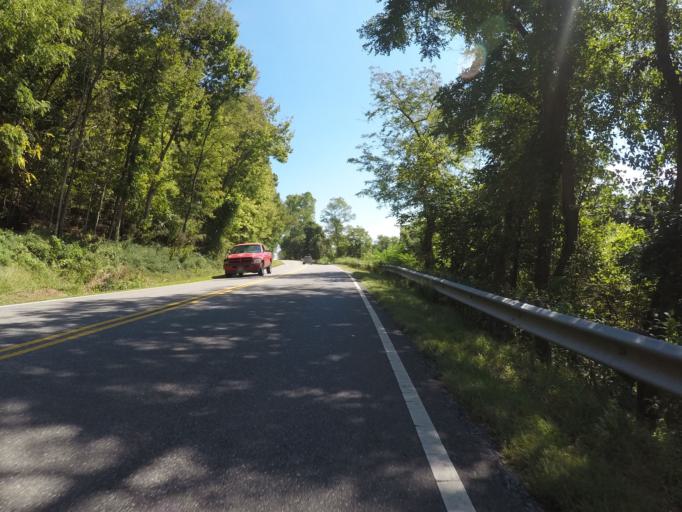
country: US
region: West Virginia
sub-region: Wayne County
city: Ceredo
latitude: 38.4060
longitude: -82.5654
